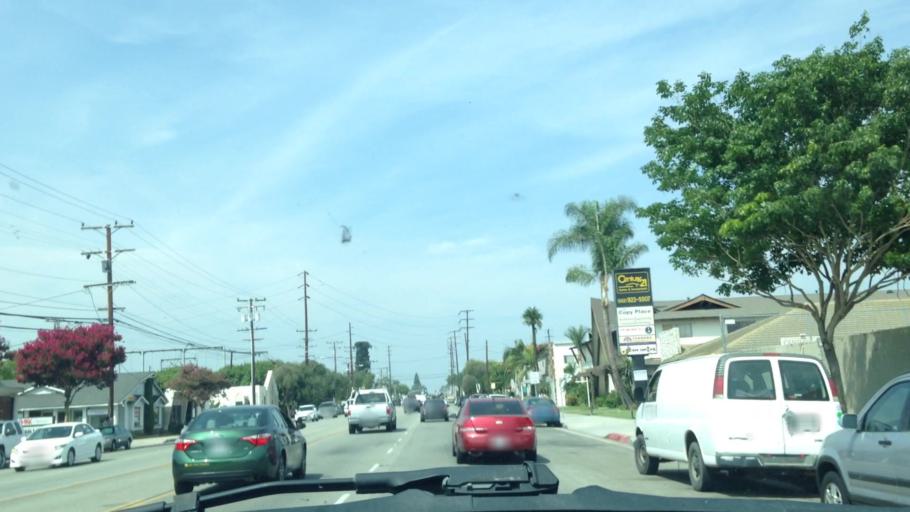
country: US
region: California
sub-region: Los Angeles County
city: Downey
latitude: 33.9384
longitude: -118.1411
